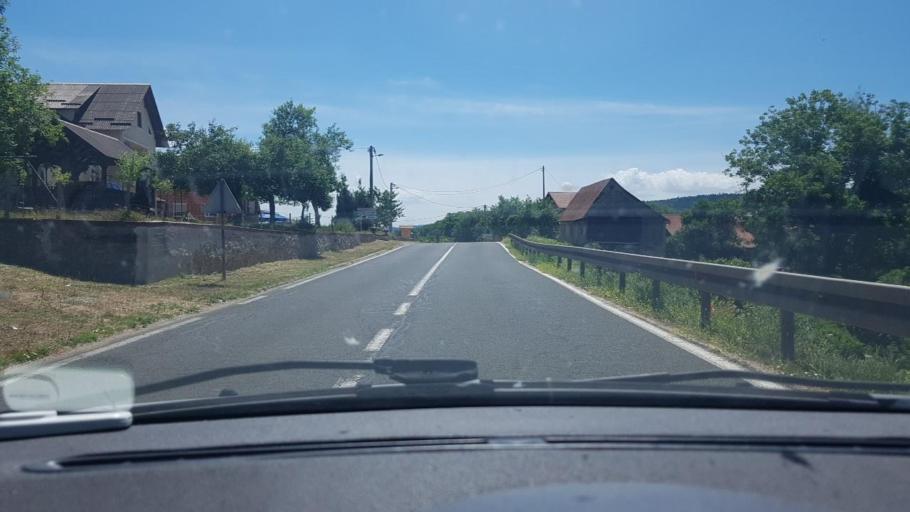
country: HR
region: Licko-Senjska
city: Otocac
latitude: 44.8784
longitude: 15.2020
